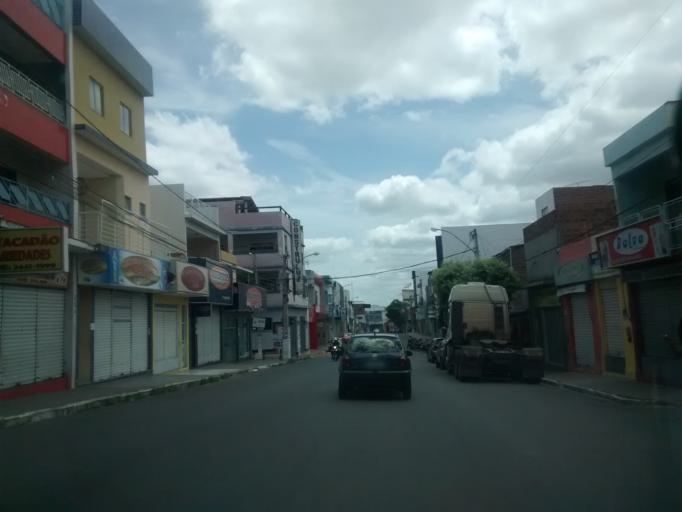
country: BR
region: Bahia
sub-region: Brumado
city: Brumado
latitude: -14.2088
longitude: -41.6681
